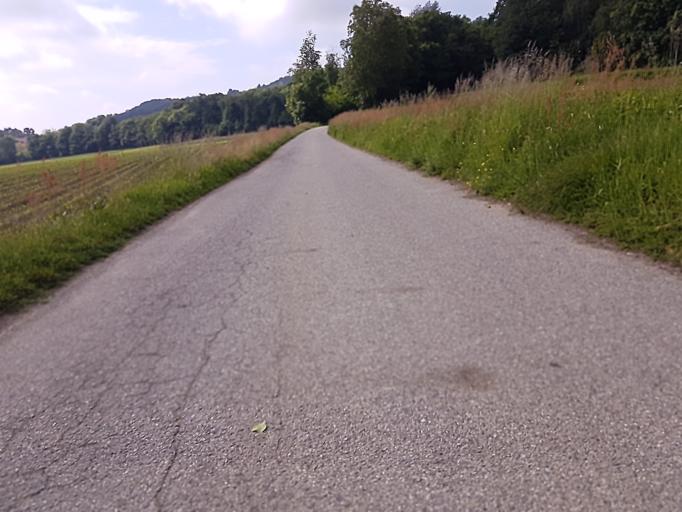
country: IT
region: Piedmont
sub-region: Provincia di Torino
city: Vialfre
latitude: 45.3858
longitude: 7.8251
